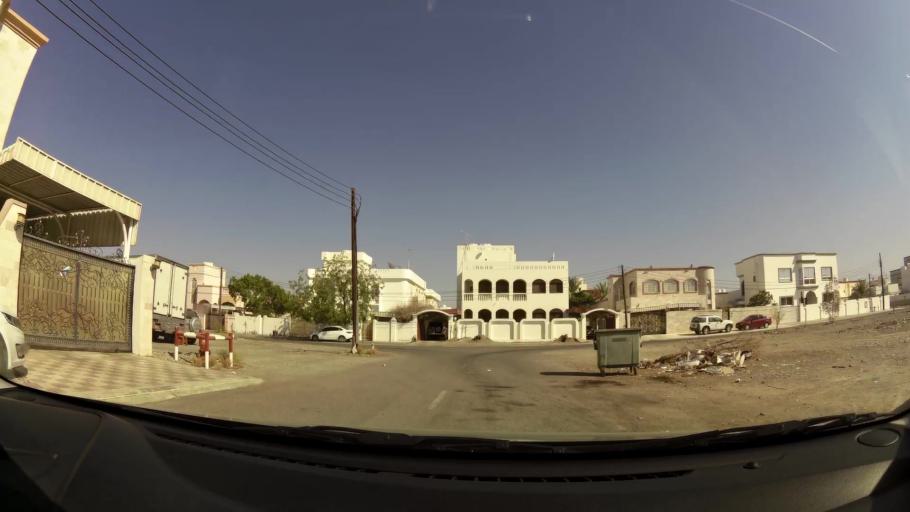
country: OM
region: Muhafazat Masqat
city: As Sib al Jadidah
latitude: 23.6317
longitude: 58.2058
